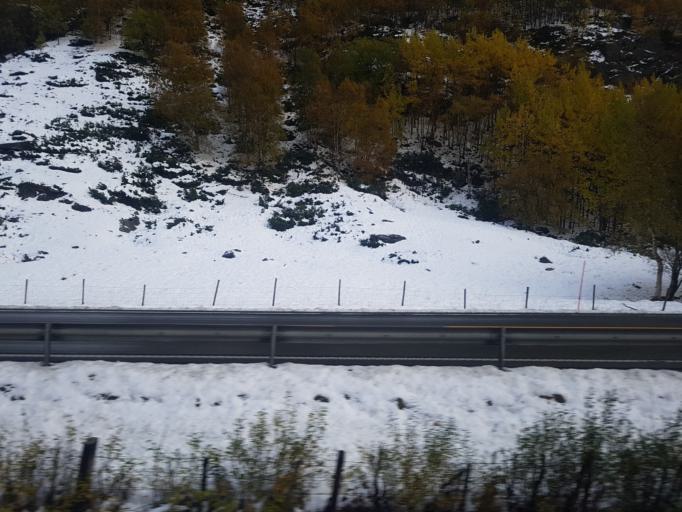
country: NO
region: Sor-Trondelag
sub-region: Oppdal
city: Oppdal
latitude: 62.4211
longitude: 9.6173
